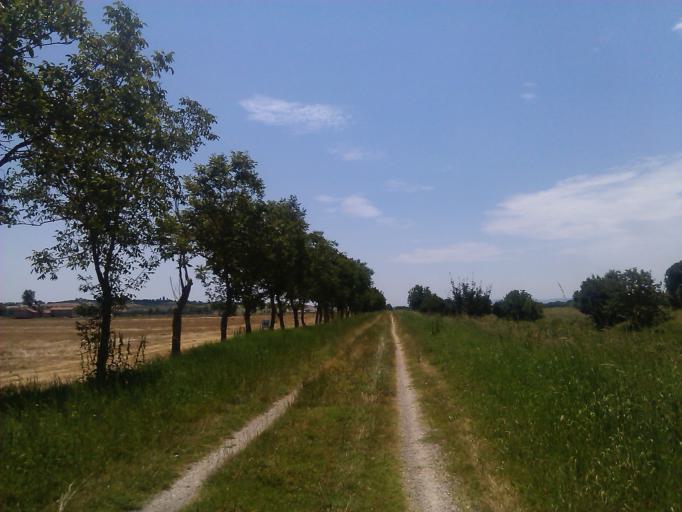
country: IT
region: Tuscany
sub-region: Province of Arezzo
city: Cesa
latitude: 43.3083
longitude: 11.8390
